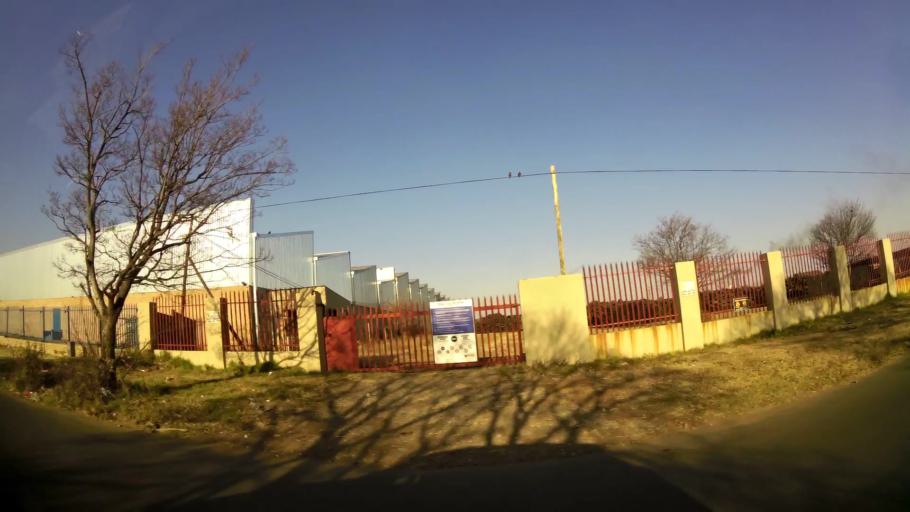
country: ZA
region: Gauteng
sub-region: West Rand District Municipality
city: Randfontein
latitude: -26.1962
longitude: 27.6843
